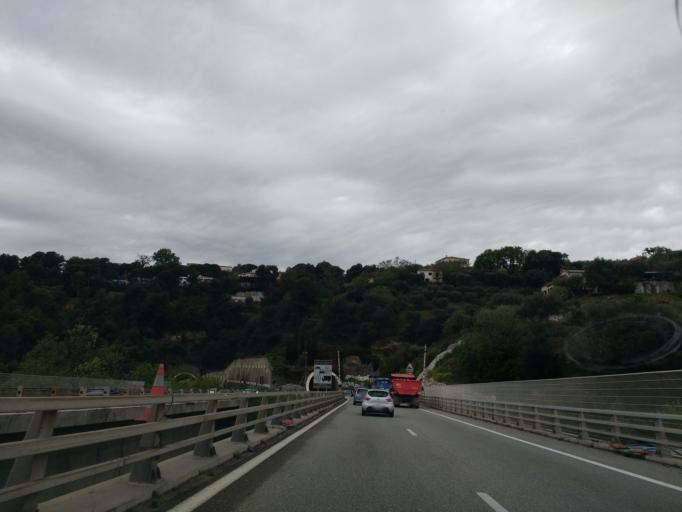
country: FR
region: Provence-Alpes-Cote d'Azur
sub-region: Departement des Alpes-Maritimes
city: Colomars
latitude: 43.7222
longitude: 7.2204
